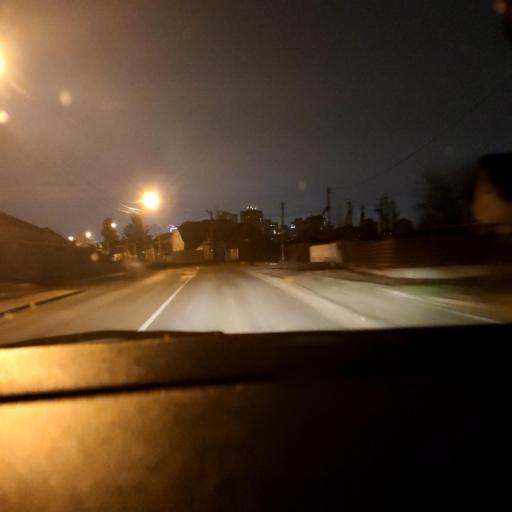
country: RU
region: Voronezj
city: Podgornoye
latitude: 51.7287
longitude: 39.1382
